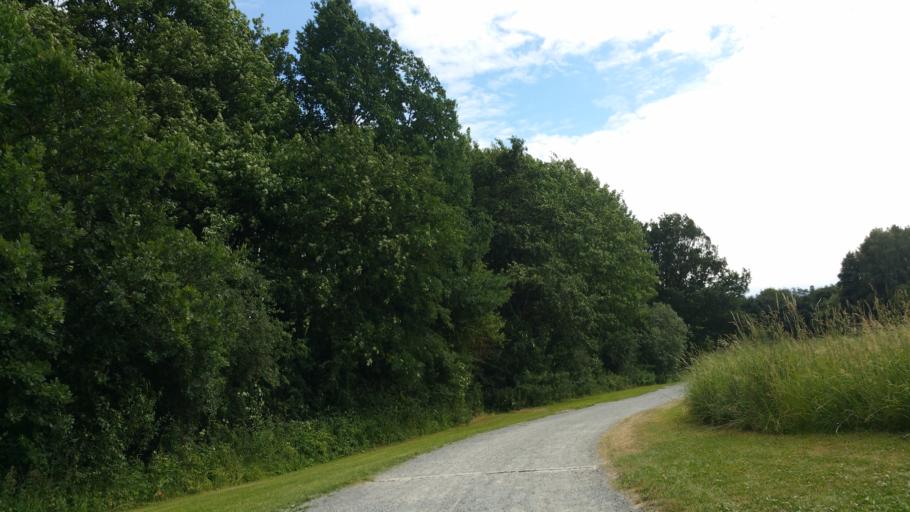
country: DE
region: Bavaria
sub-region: Upper Franconia
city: Hof
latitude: 50.2820
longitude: 11.9060
